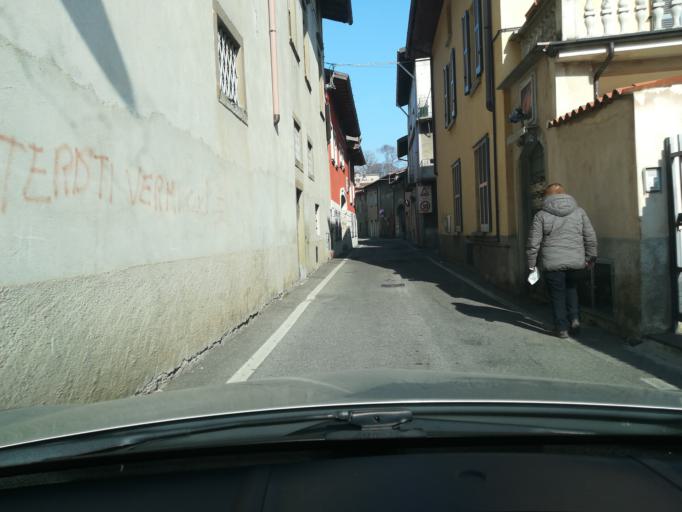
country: IT
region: Lombardy
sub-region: Provincia di Bergamo
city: Stezzano
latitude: 45.6492
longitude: 9.6553
